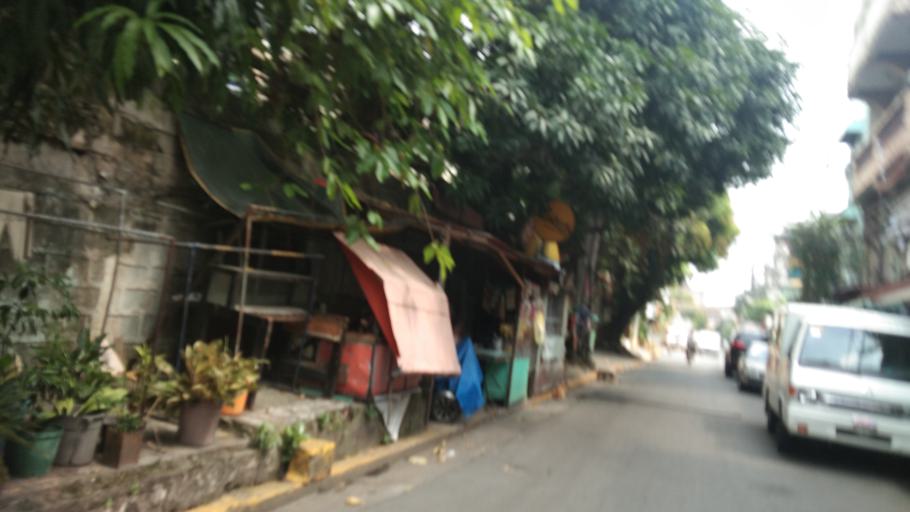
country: PH
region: Metro Manila
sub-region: City of Manila
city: Quiapo
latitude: 14.5766
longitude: 121.0003
